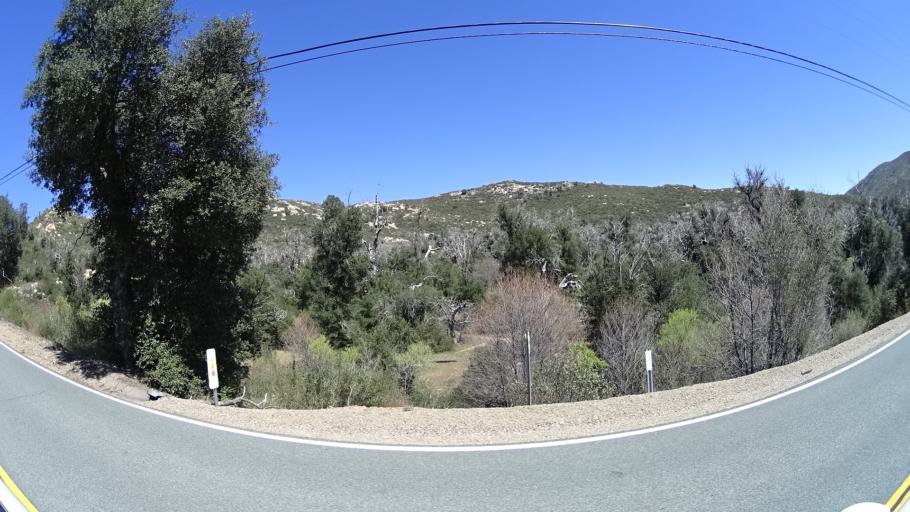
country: US
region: California
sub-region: San Diego County
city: Descanso
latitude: 32.9382
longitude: -116.5638
